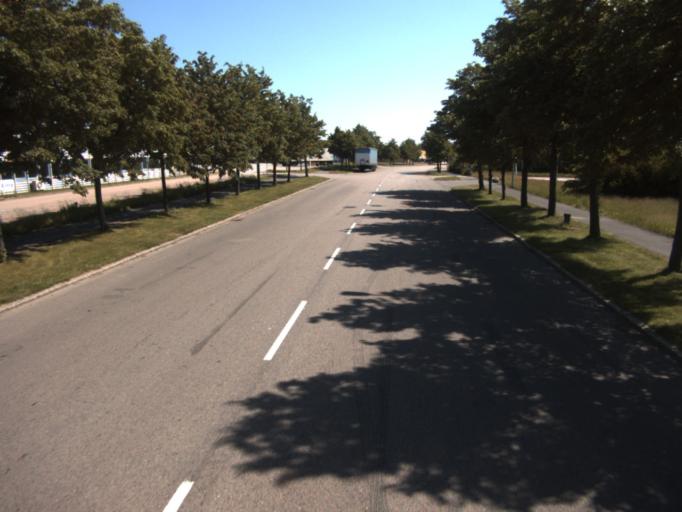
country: SE
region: Skane
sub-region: Helsingborg
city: Gantofta
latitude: 56.0059
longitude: 12.7706
